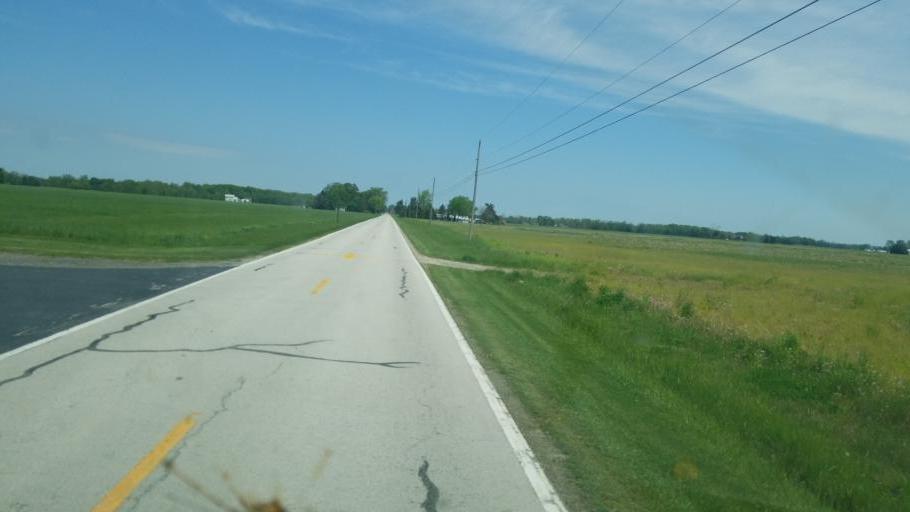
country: US
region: Ohio
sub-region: Sandusky County
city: Stony Prairie
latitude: 41.4068
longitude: -83.2022
